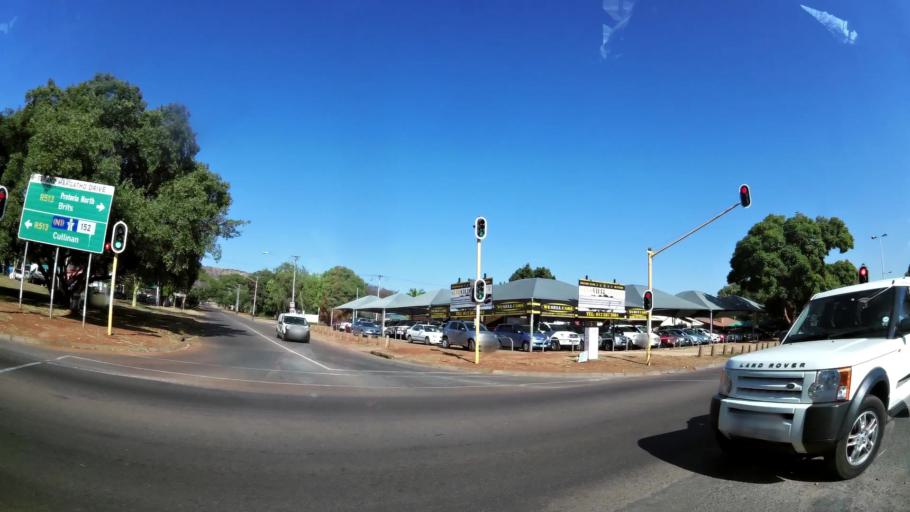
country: ZA
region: Gauteng
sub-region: City of Tshwane Metropolitan Municipality
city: Pretoria
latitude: -25.6798
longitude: 28.2116
